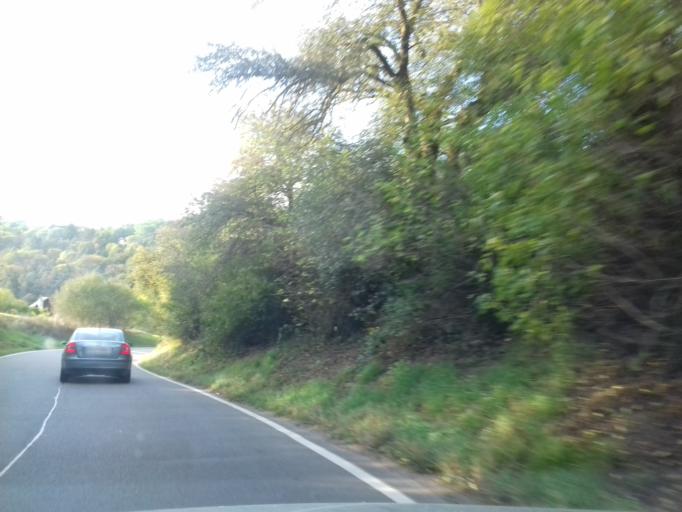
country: CZ
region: Central Bohemia
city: Kamenny Privoz
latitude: 49.8721
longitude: 14.5038
